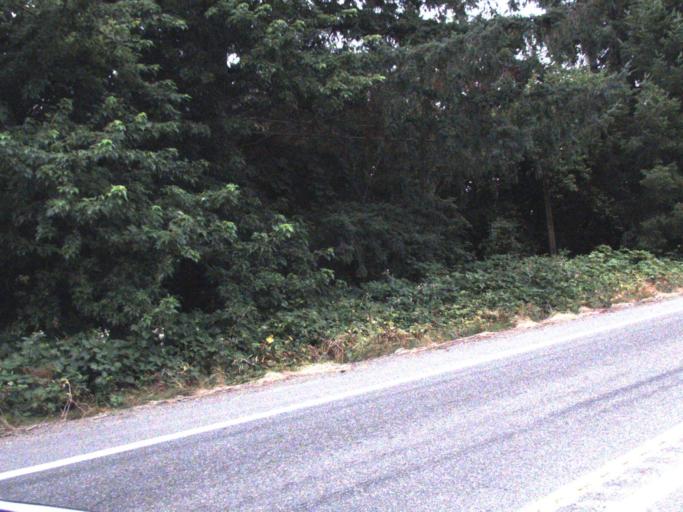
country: US
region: Washington
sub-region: King County
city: Fall City
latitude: 47.5629
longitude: -121.8660
